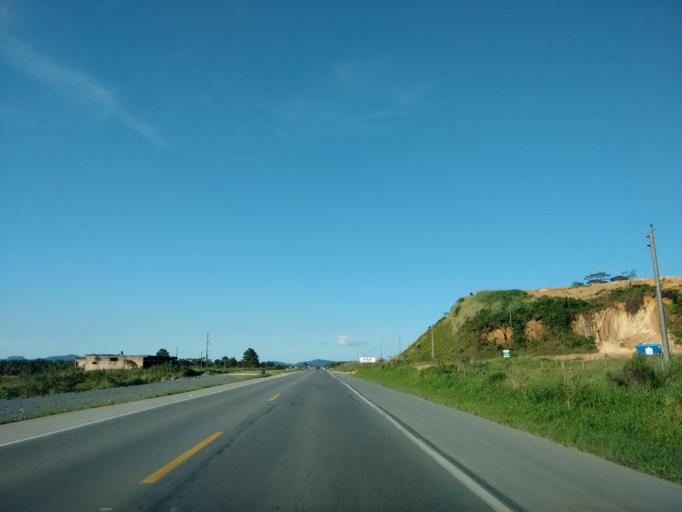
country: BR
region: Santa Catarina
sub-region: Guaramirim
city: Guaramirim
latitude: -26.4524
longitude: -48.8972
